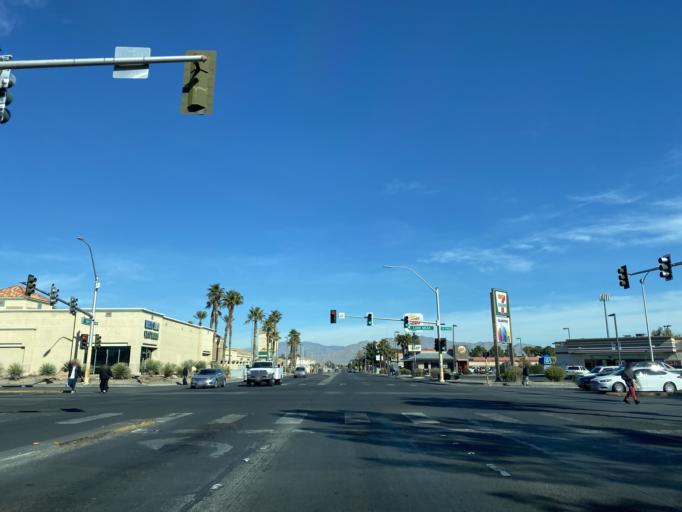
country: US
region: Nevada
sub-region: Clark County
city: Las Vegas
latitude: 36.1955
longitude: -115.2239
